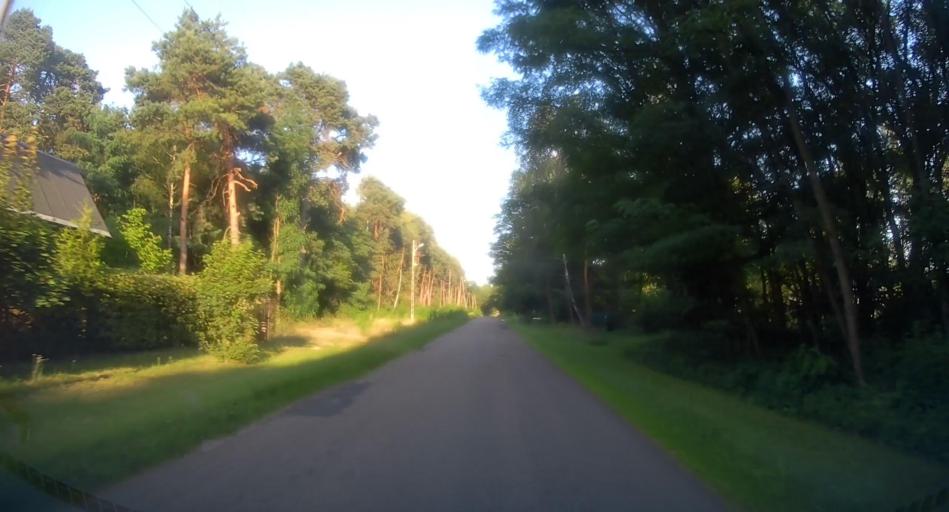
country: PL
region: Lodz Voivodeship
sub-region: Powiat skierniewicki
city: Kowiesy
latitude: 51.9050
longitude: 20.3551
